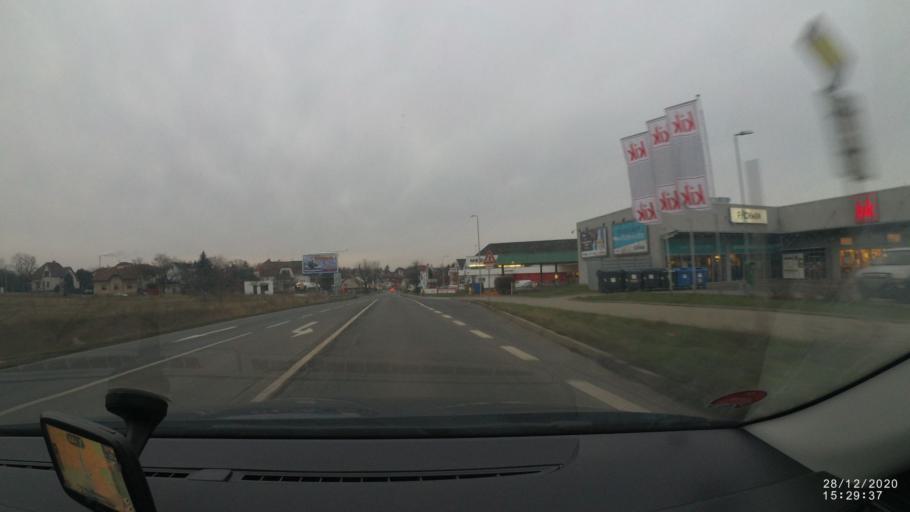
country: CZ
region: Praha
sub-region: Praha 14
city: Dolni Pocernice
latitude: 50.0849
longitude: 14.5786
